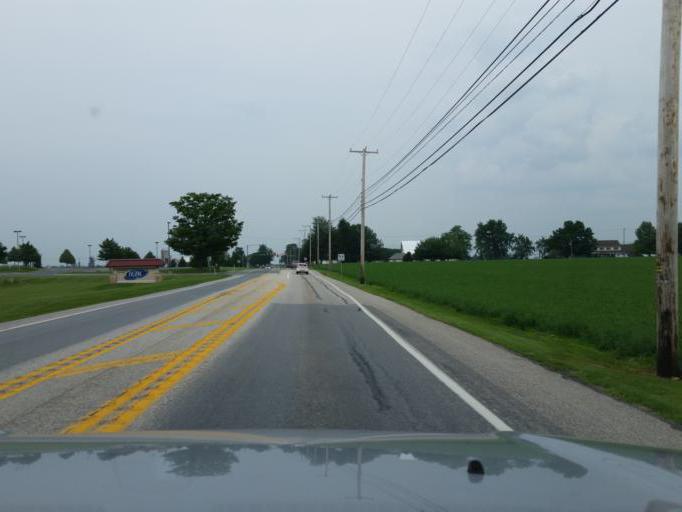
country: US
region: Pennsylvania
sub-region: Lancaster County
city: Salunga
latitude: 40.1278
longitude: -76.4553
